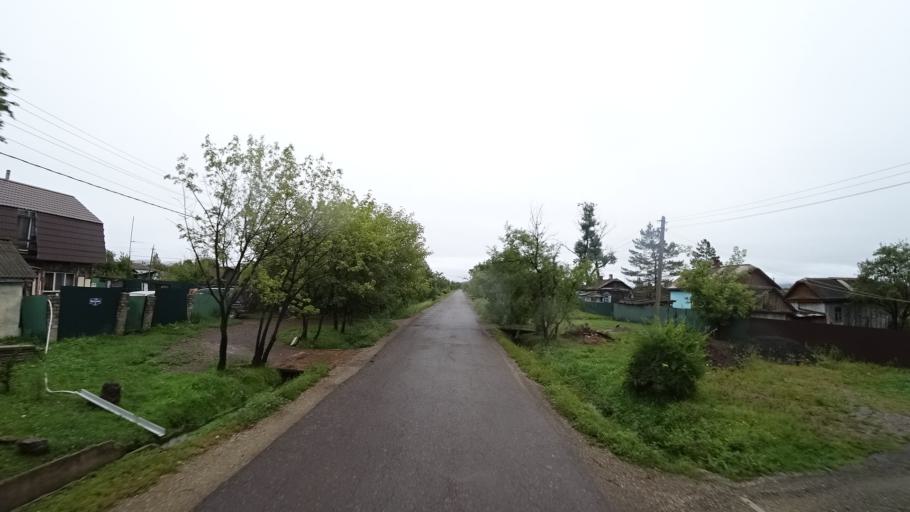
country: RU
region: Primorskiy
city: Monastyrishche
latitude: 44.2028
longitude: 132.4598
